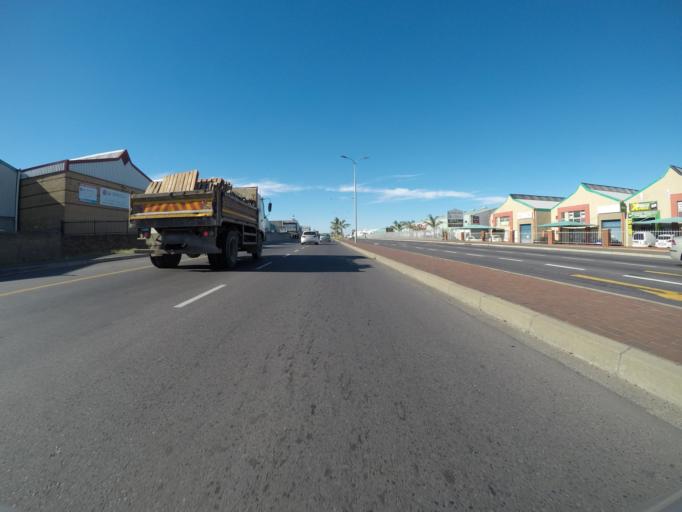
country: ZA
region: Western Cape
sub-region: City of Cape Town
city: Kraaifontein
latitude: -33.9031
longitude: 18.6687
